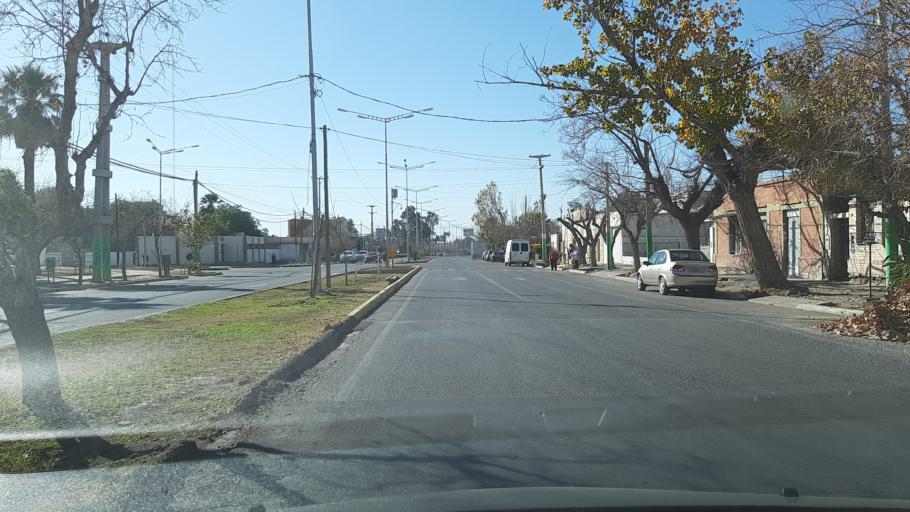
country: AR
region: San Juan
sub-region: Departamento de Rivadavia
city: Rivadavia
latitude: -31.5251
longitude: -68.6279
